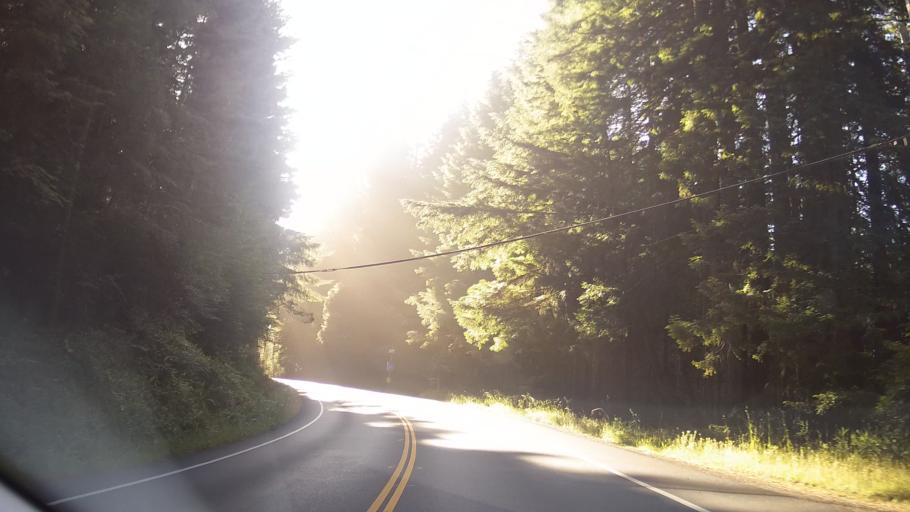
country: US
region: California
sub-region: Mendocino County
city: Fort Bragg
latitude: 39.4048
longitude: -123.7215
